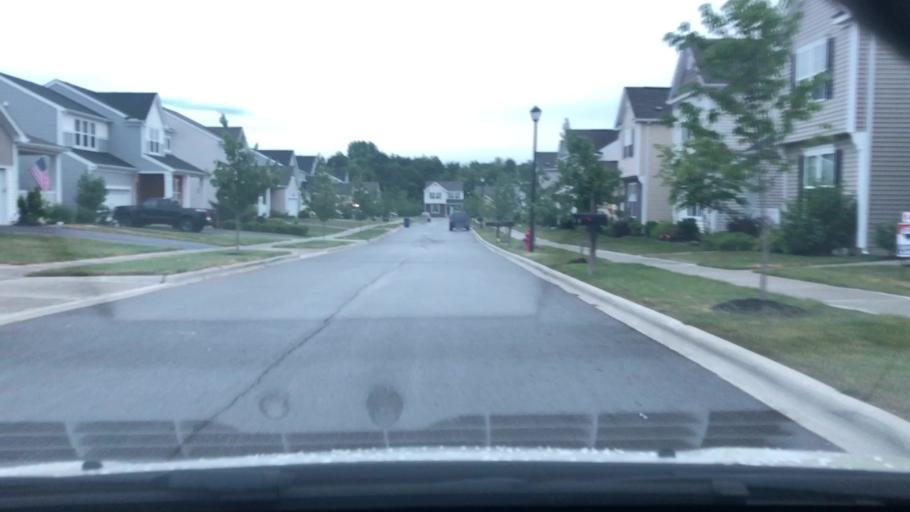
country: US
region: Ohio
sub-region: Franklin County
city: New Albany
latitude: 40.0984
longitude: -82.8547
